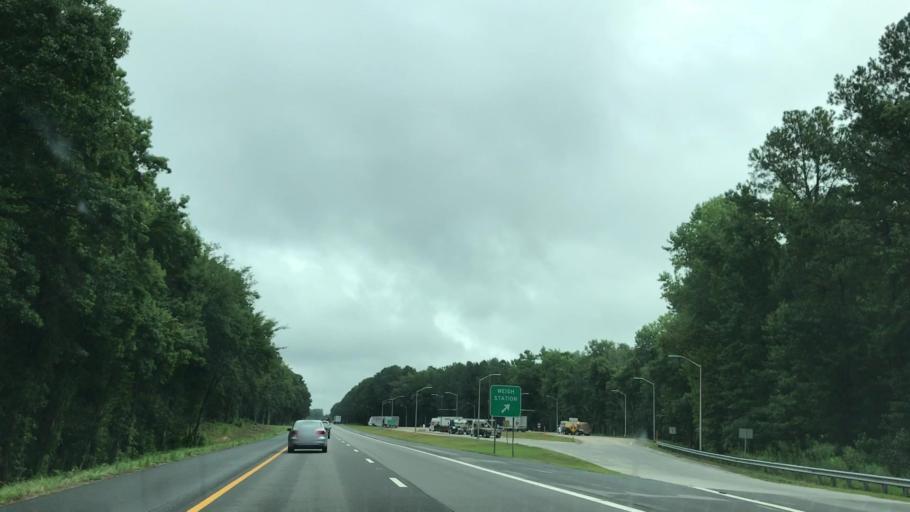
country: US
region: North Carolina
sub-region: Halifax County
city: Enfield
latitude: 36.1455
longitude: -77.7858
